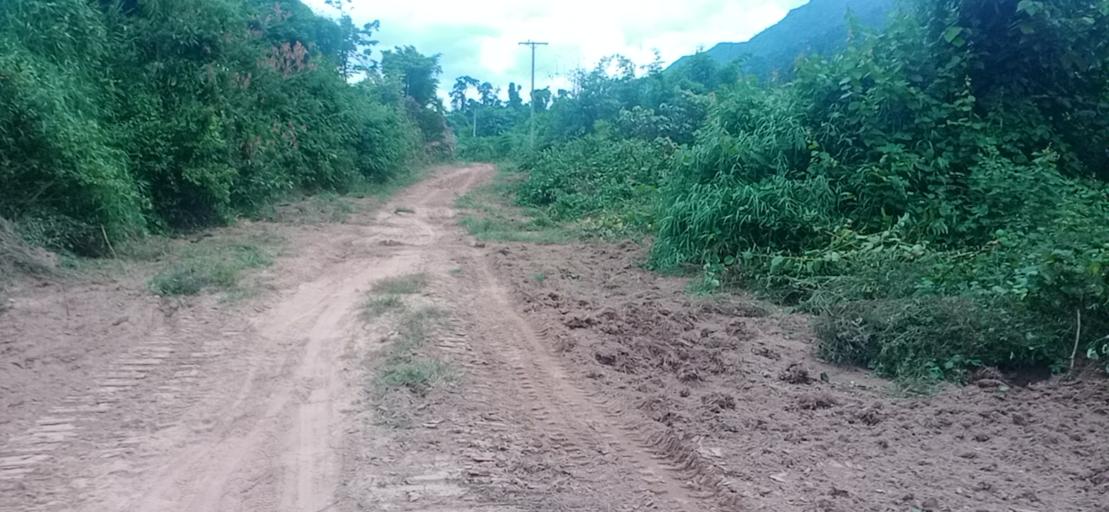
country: TH
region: Changwat Bueng Kan
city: Pak Khat
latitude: 18.5582
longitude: 103.2373
